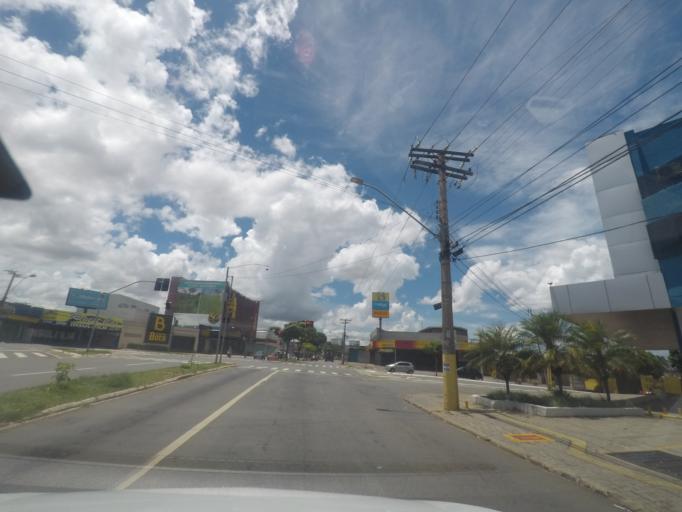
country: BR
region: Goias
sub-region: Goiania
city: Goiania
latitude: -16.6745
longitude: -49.2951
